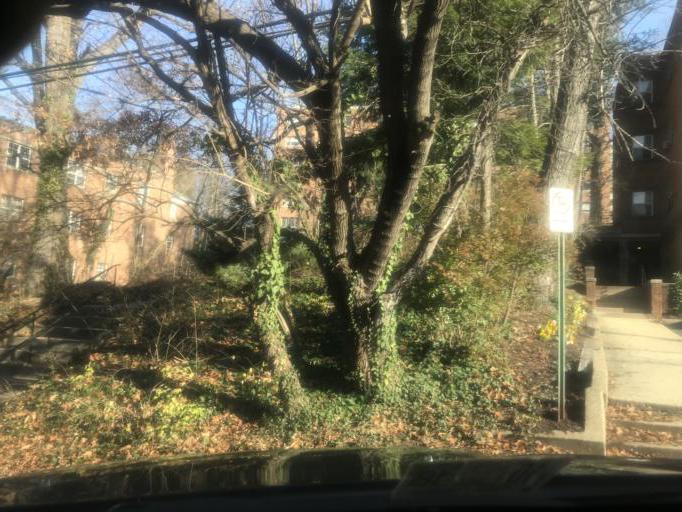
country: US
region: Virginia
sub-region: Arlington County
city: Arlington
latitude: 38.8895
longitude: -77.0746
